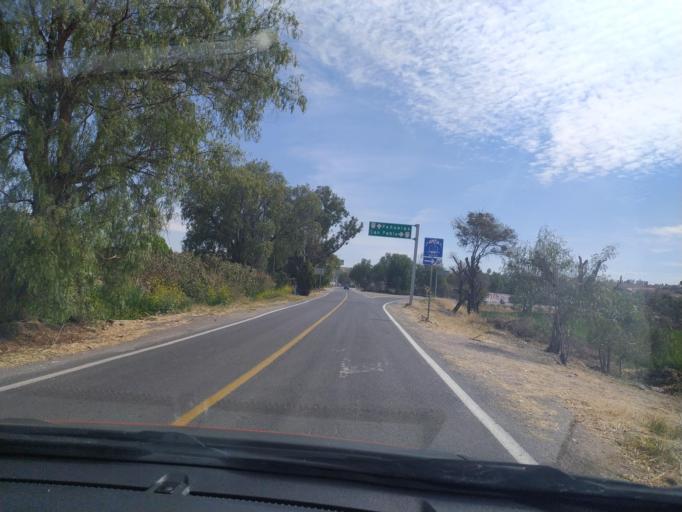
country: MX
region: Guanajuato
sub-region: San Francisco del Rincon
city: San Ignacio de Hidalgo
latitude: 20.8816
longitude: -101.8614
